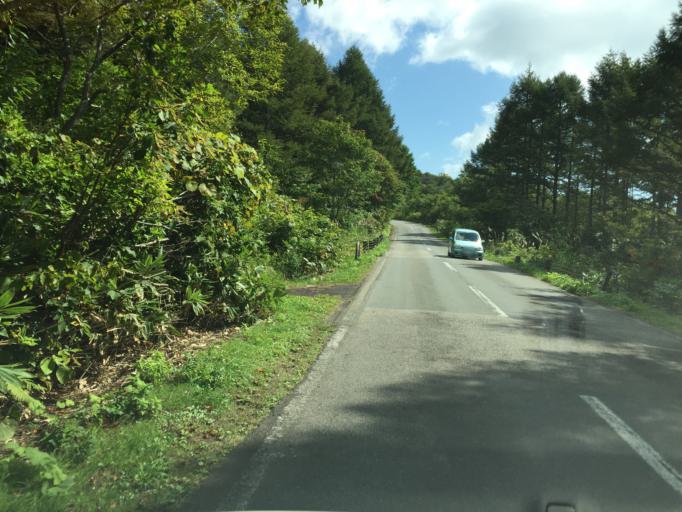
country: JP
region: Fukushima
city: Inawashiro
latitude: 37.6049
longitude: 140.0463
